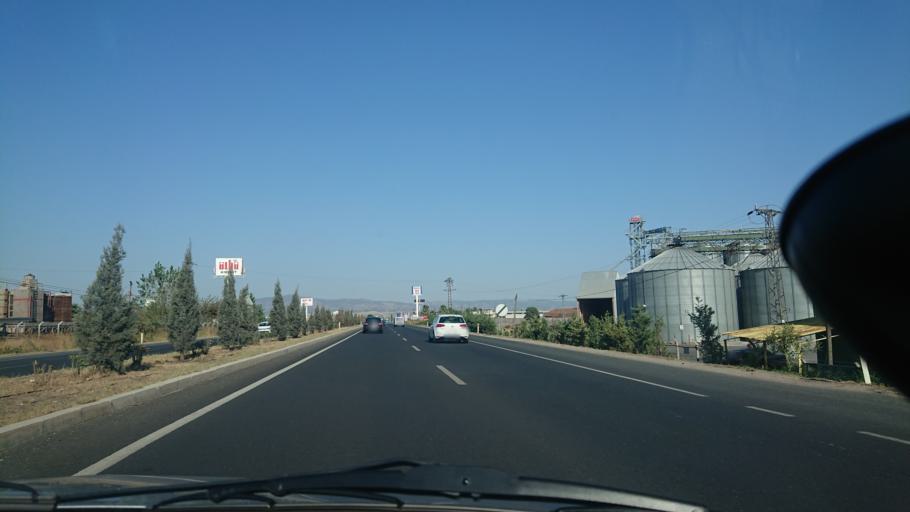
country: TR
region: Manisa
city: Salihli
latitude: 38.5043
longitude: 28.2230
